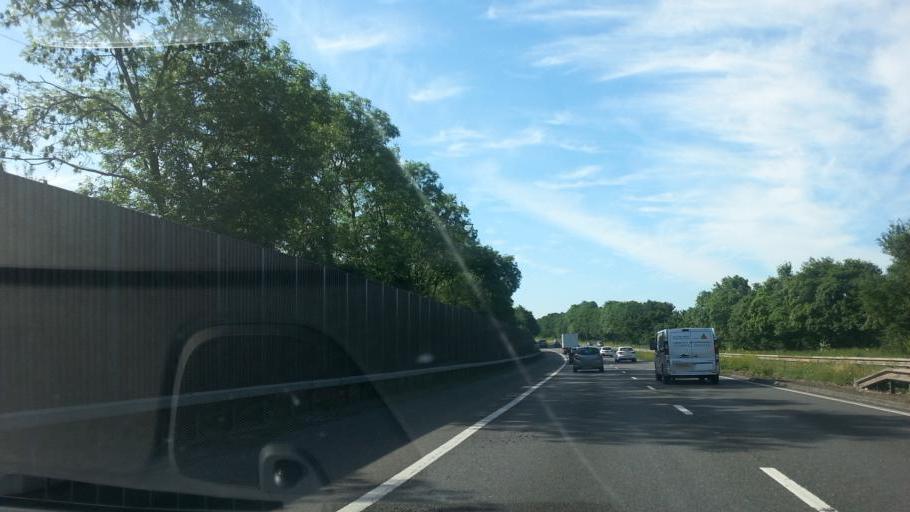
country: GB
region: England
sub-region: Hertfordshire
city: Stevenage
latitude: 51.9111
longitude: -0.2278
